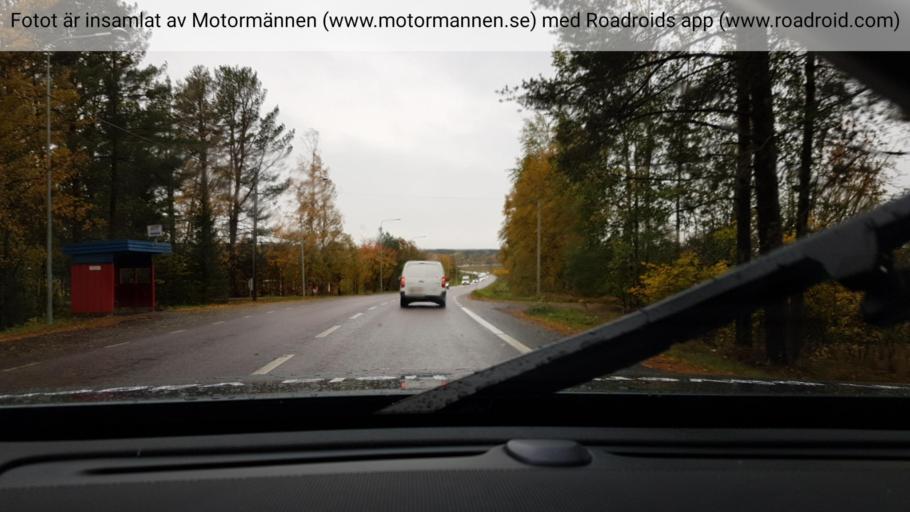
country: SE
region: Norrbotten
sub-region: Lulea Kommun
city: Bergnaset
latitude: 65.5808
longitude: 22.0649
